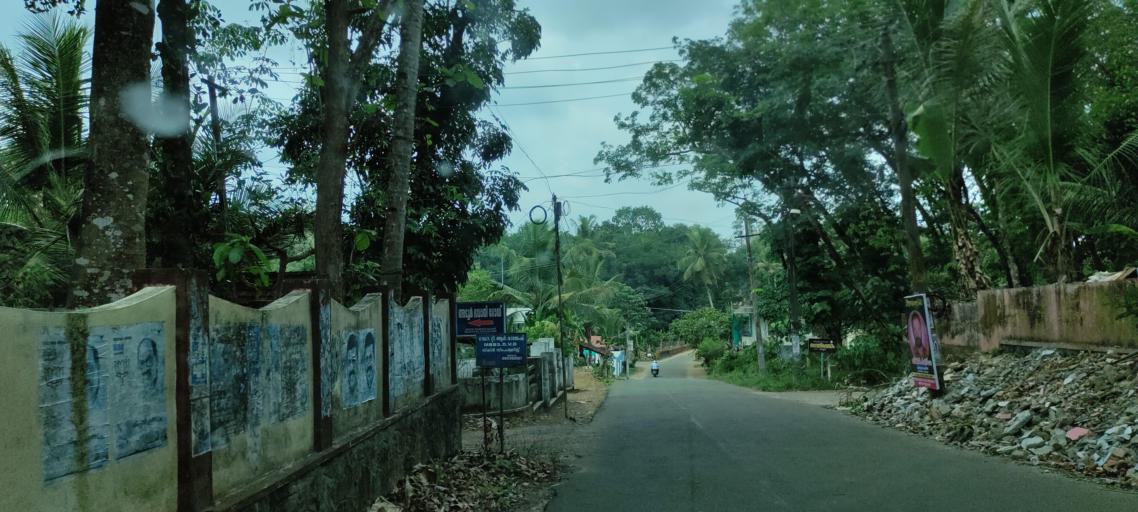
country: IN
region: Kerala
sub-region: Pattanamtitta
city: Adur
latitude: 9.1682
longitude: 76.7359
